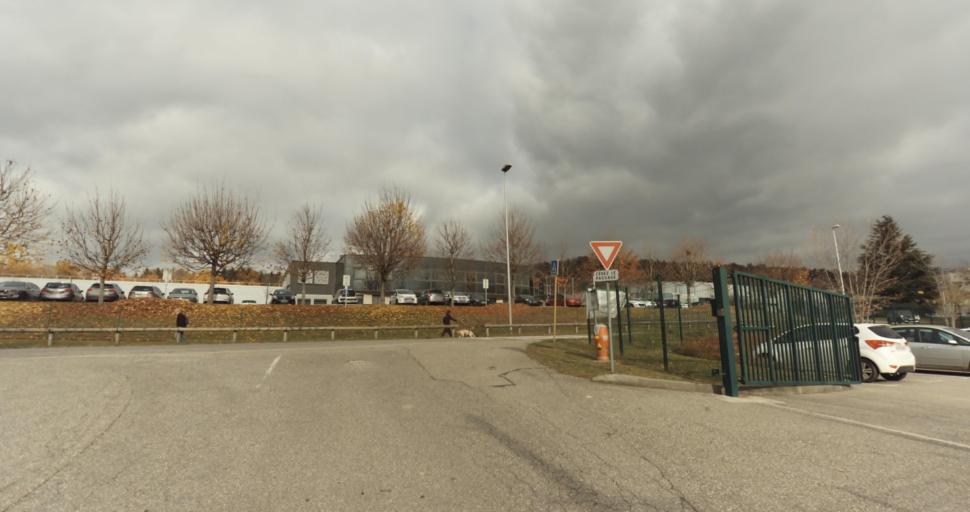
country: FR
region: Rhone-Alpes
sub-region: Departement de la Haute-Savoie
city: Pringy
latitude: 45.9437
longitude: 6.1303
